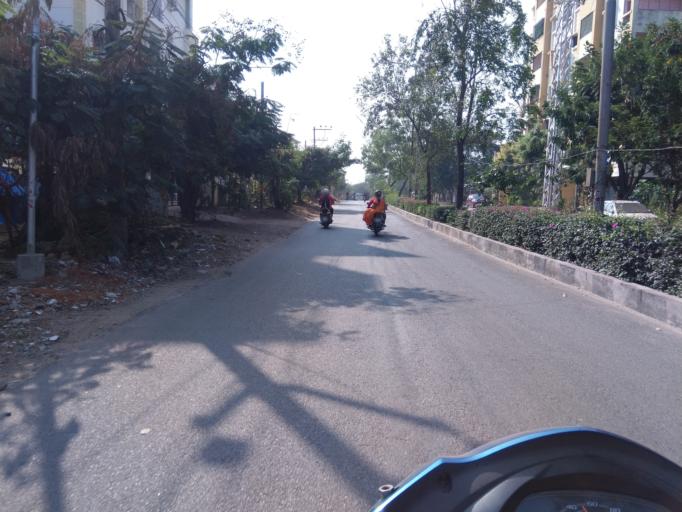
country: IN
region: Telangana
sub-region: Rangareddi
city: Kukatpalli
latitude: 17.4782
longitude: 78.3948
